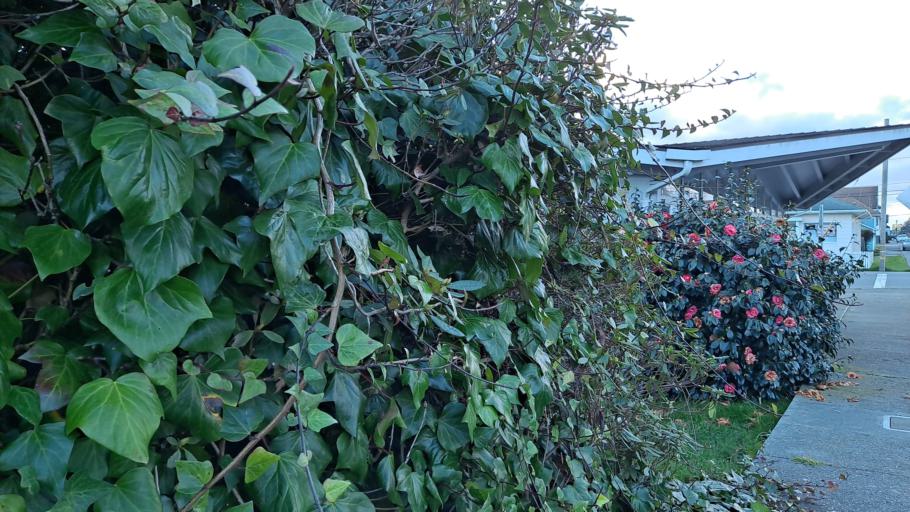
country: US
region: California
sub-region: Humboldt County
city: Fortuna
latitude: 40.5988
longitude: -124.1519
